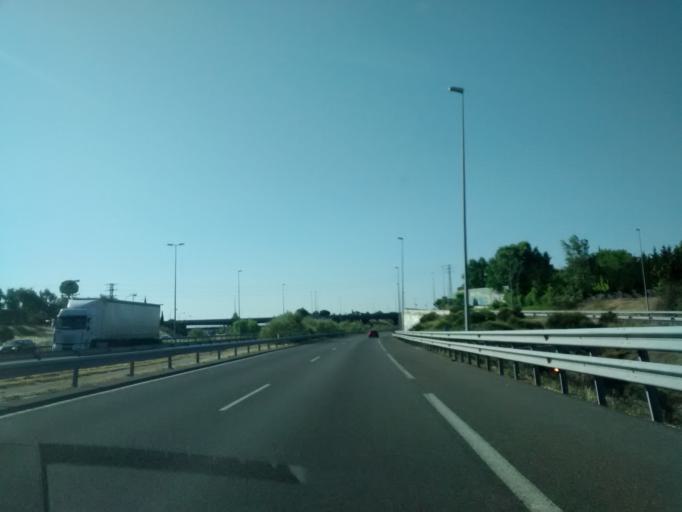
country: ES
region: Madrid
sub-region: Provincia de Madrid
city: Majadahonda
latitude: 40.4576
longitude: -3.8805
